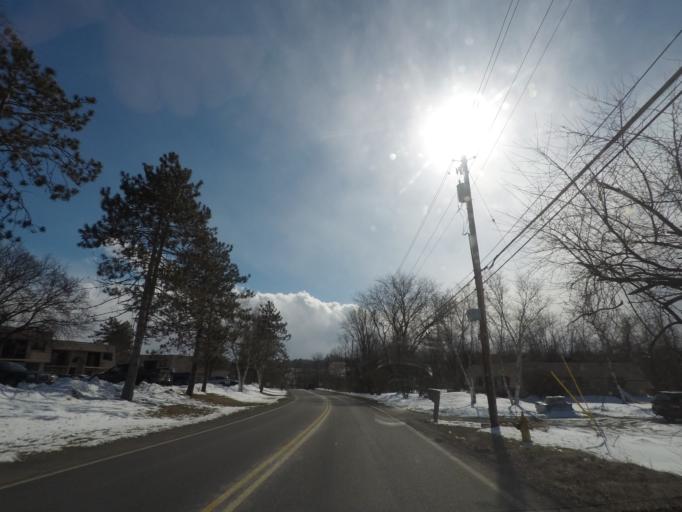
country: US
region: New York
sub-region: Albany County
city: McKownville
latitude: 42.6515
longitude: -73.8510
